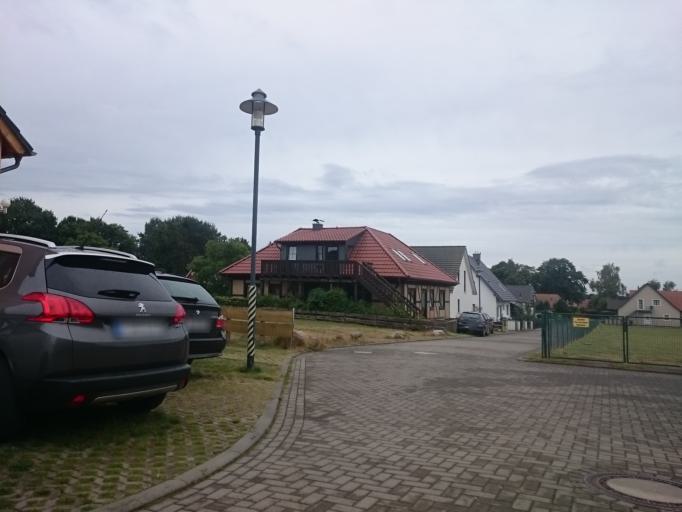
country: DE
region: Mecklenburg-Vorpommern
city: Koserow
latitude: 54.0515
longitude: 14.0023
